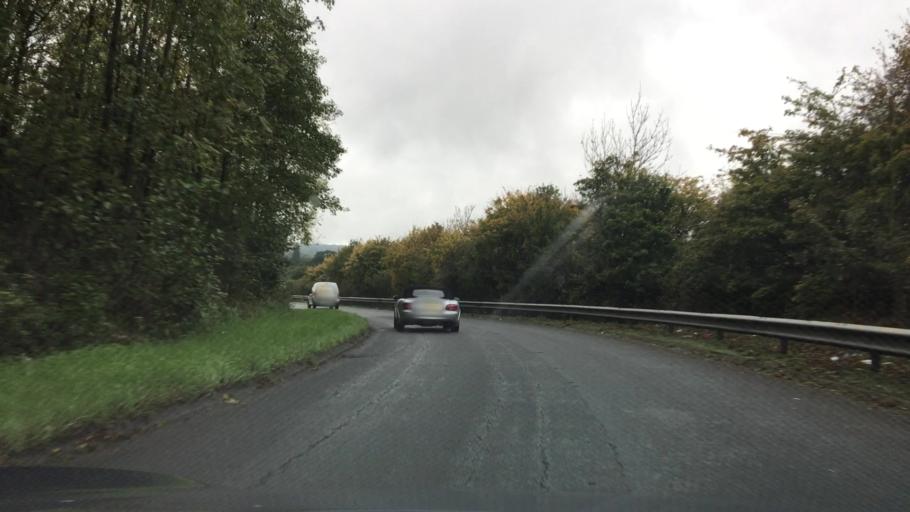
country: GB
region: England
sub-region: Worcestershire
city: Alvechurch
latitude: 52.3614
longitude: -1.9498
